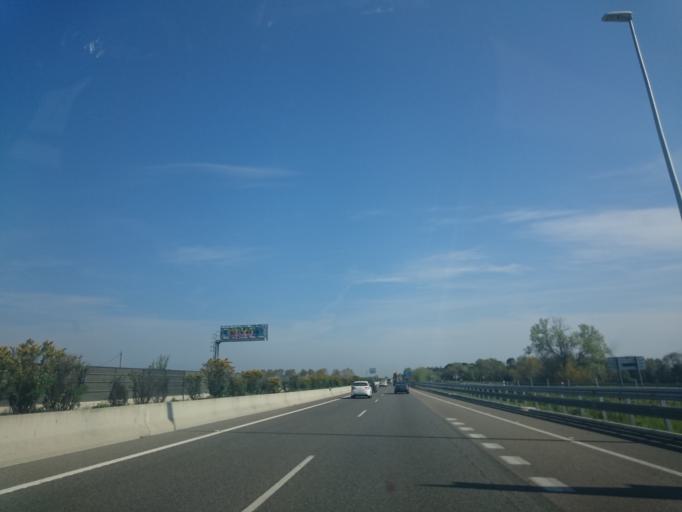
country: ES
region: Catalonia
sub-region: Provincia de Girona
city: Vilobi d'Onyar
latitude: 41.8726
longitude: 2.7787
